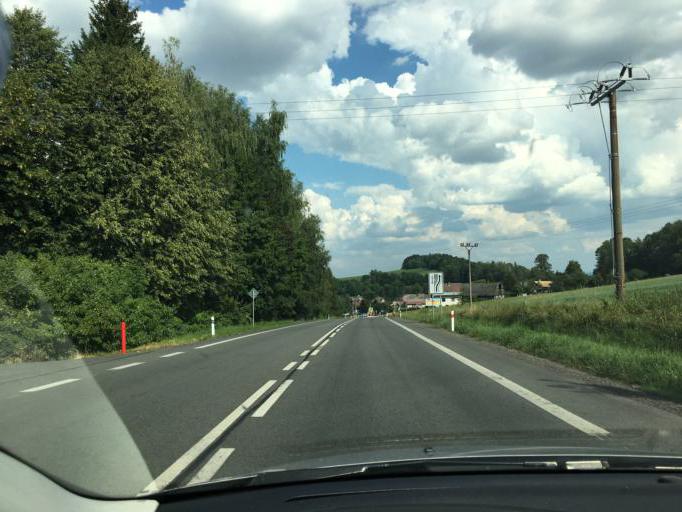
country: CZ
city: Horni Branna
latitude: 50.6217
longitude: 15.5519
